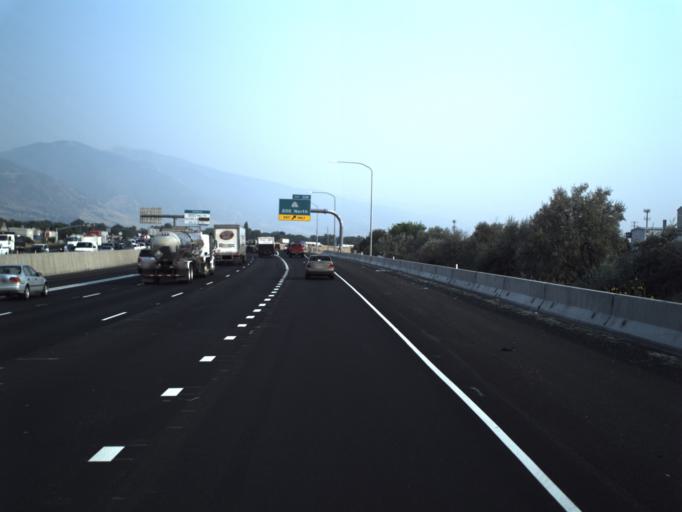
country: US
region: Utah
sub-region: Davis County
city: Kaysville
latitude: 41.0426
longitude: -111.9545
